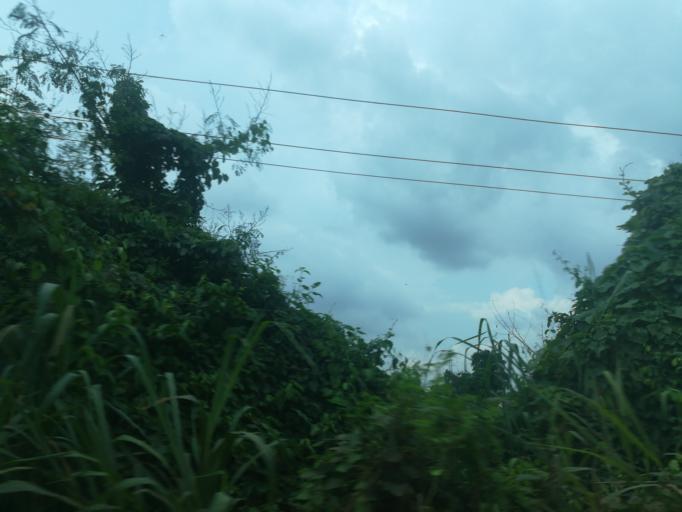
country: NG
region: Lagos
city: Ikorodu
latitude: 6.6374
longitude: 3.5427
